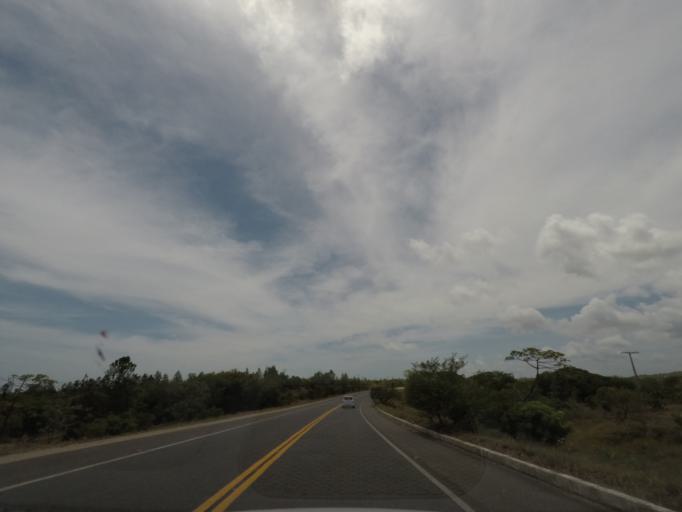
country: BR
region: Bahia
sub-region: Conde
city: Conde
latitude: -11.8656
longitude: -37.6314
